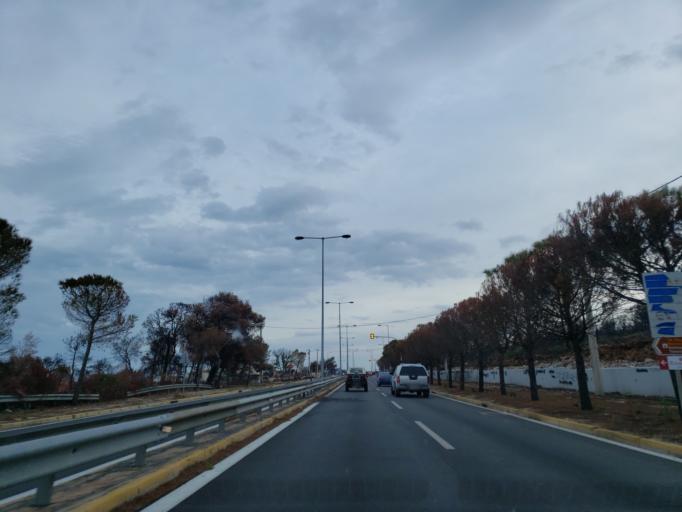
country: GR
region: Attica
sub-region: Nomarchia Anatolikis Attikis
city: Neos Voutzas
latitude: 38.0472
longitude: 23.9880
